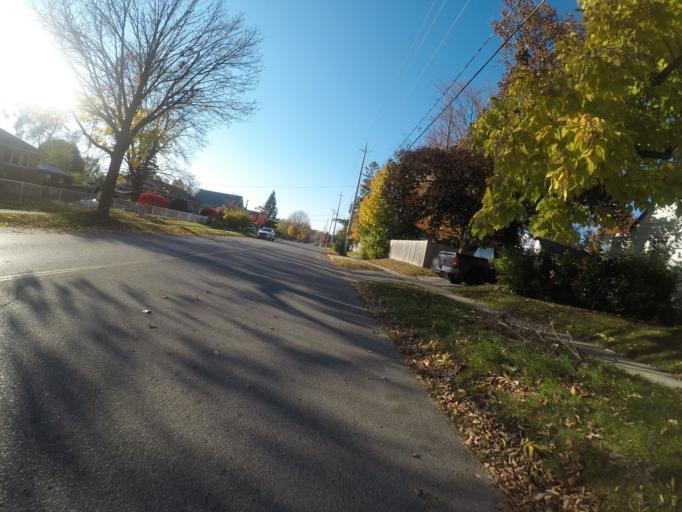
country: CA
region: Ontario
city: Kitchener
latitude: 43.4309
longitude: -80.4534
